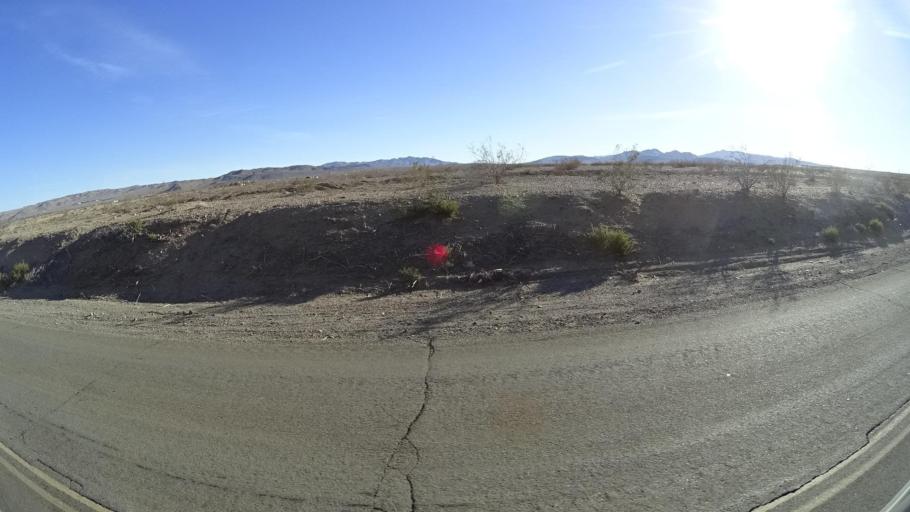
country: US
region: California
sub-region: Kern County
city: China Lake Acres
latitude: 35.6080
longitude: -117.7258
